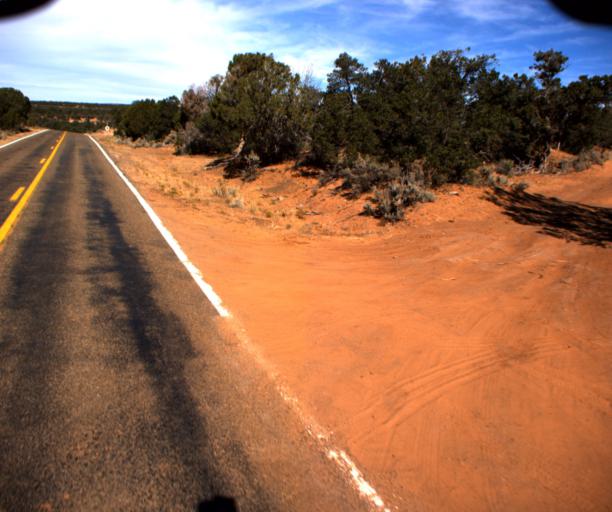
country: US
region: Arizona
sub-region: Navajo County
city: Kayenta
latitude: 36.6052
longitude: -110.5001
